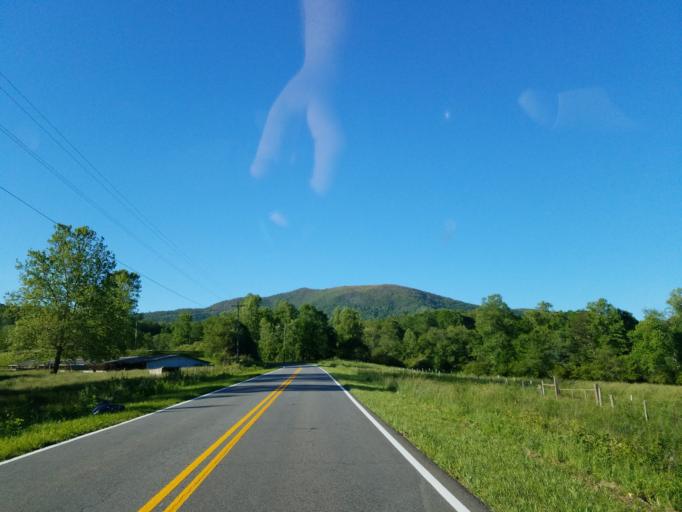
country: US
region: Georgia
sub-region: Gilmer County
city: Ellijay
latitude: 34.6713
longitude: -84.3838
